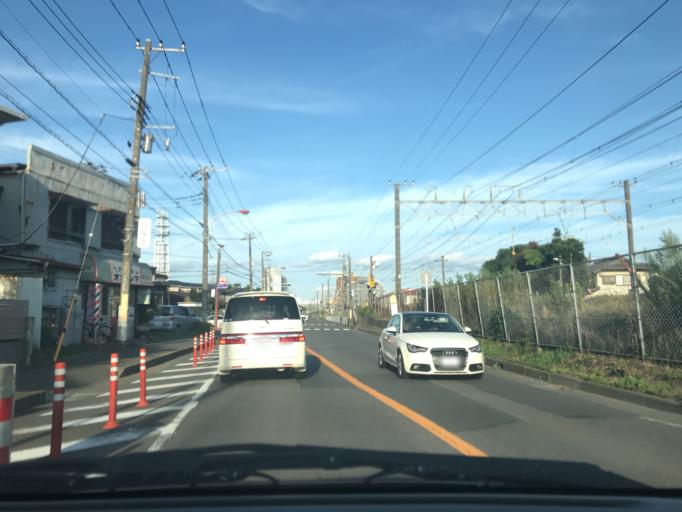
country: JP
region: Kanagawa
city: Fujisawa
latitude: 35.3383
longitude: 139.4716
